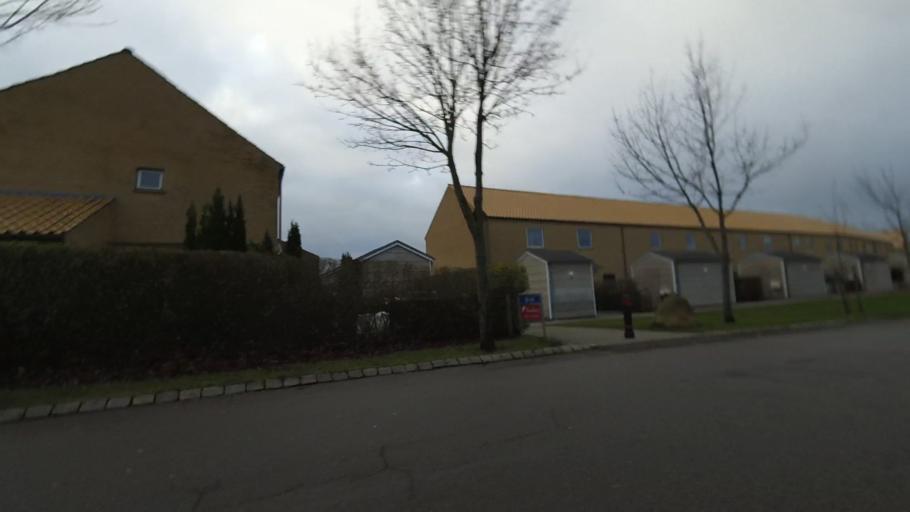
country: DK
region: Central Jutland
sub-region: Arhus Kommune
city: Marslet
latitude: 56.1032
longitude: 10.1671
